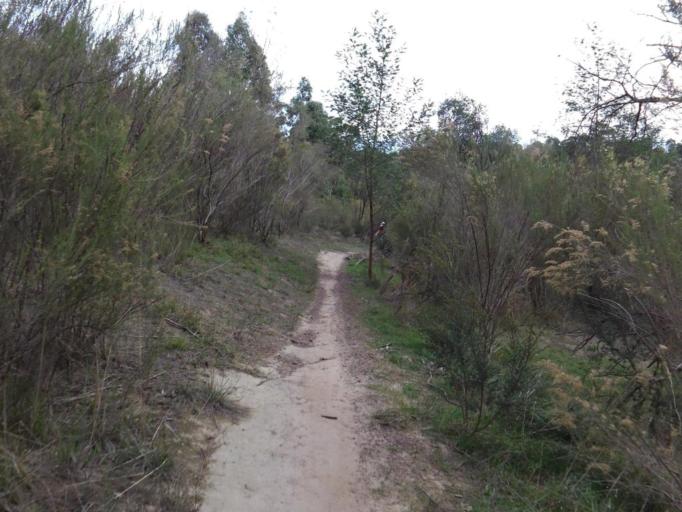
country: AU
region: Victoria
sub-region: Nillumbik
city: Eltham
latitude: -37.7460
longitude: 145.1430
